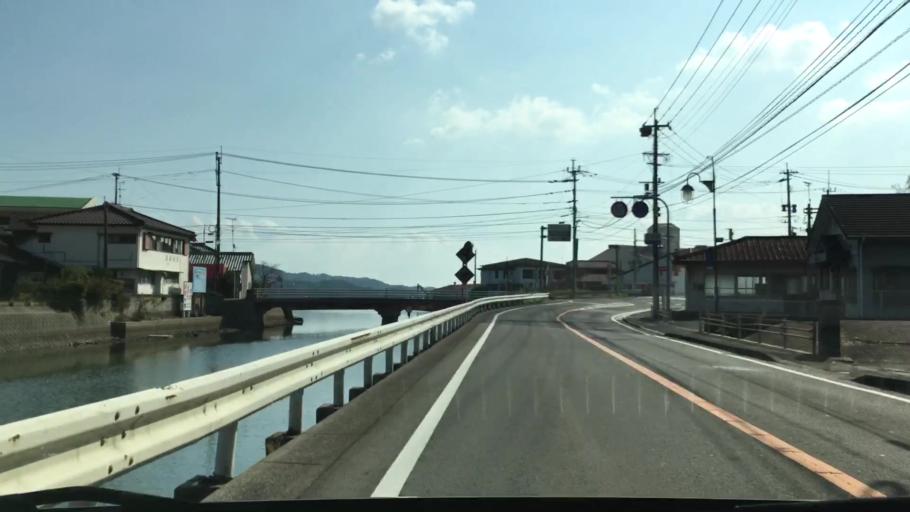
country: JP
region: Nagasaki
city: Togitsu
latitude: 32.9508
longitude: 129.7851
